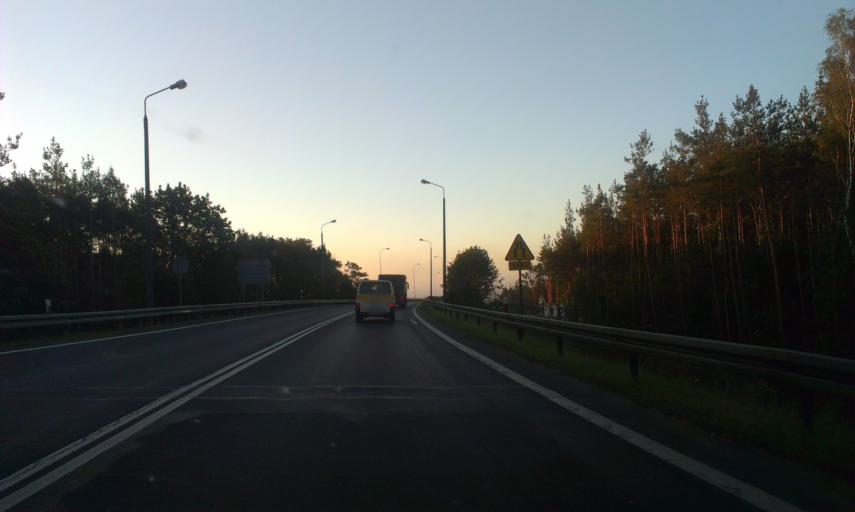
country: PL
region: Kujawsko-Pomorskie
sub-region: Powiat swiecki
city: Swiecie
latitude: 53.4012
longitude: 18.3988
